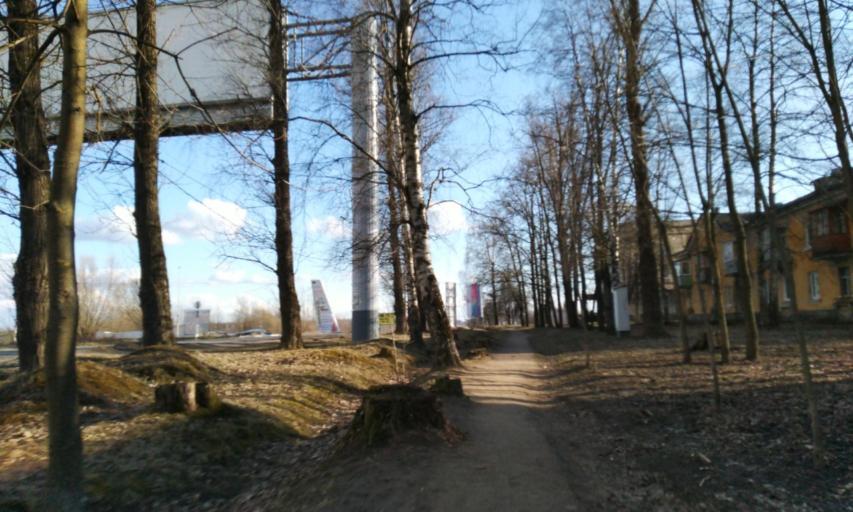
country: RU
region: Leningrad
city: Novoye Devyatkino
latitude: 60.1078
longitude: 30.5001
